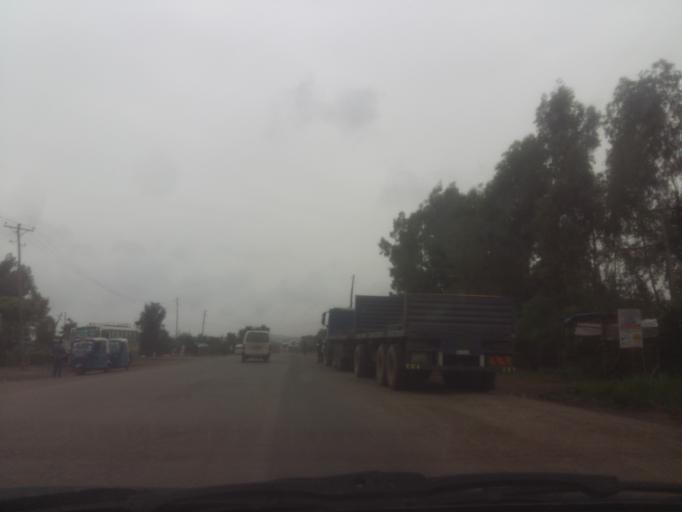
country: ET
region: Oromiya
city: Bishoftu
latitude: 8.7967
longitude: 38.8984
